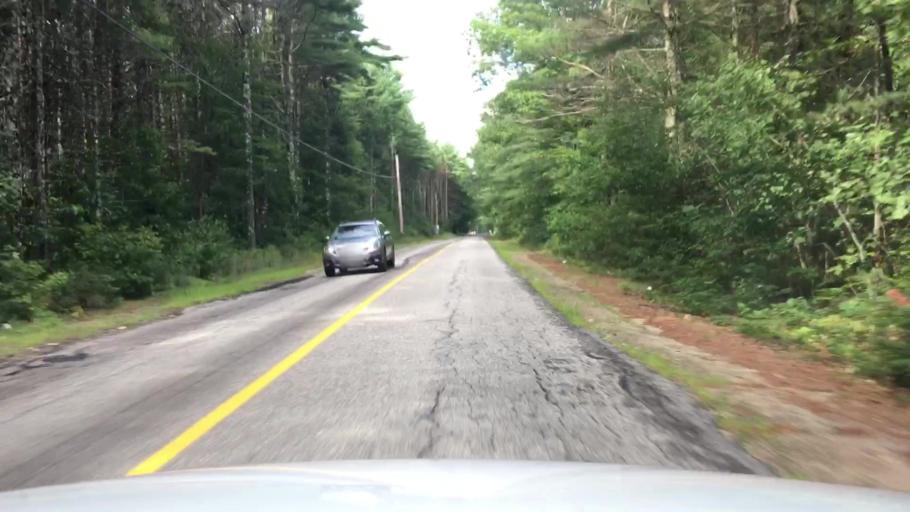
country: US
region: Maine
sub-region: York County
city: West Kennebunk
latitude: 43.4269
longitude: -70.6499
